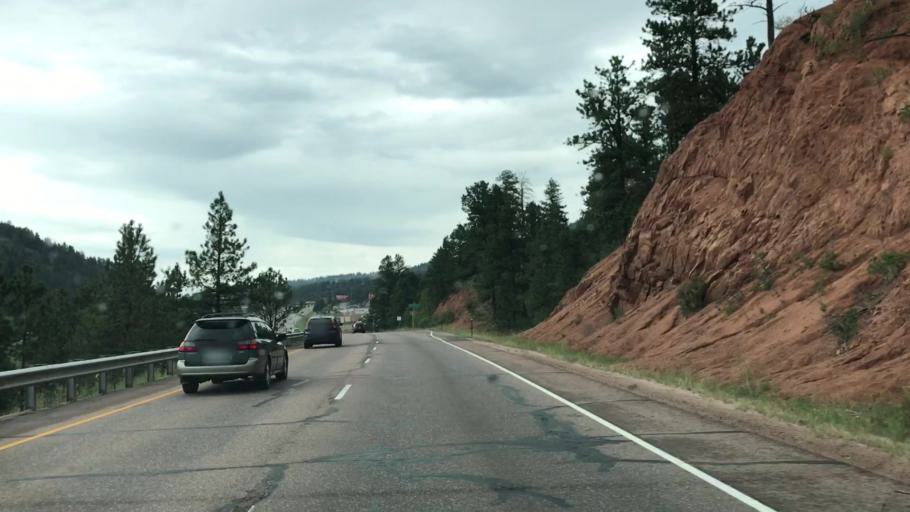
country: US
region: Colorado
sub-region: El Paso County
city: Cascade-Chipita Park
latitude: 38.9517
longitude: -105.0255
